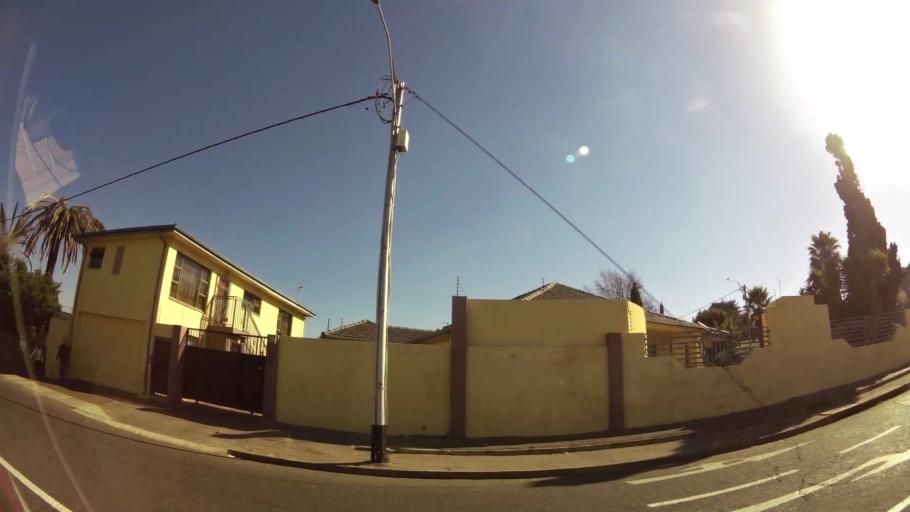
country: ZA
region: Gauteng
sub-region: City of Johannesburg Metropolitan Municipality
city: Johannesburg
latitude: -26.1930
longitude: 27.9899
